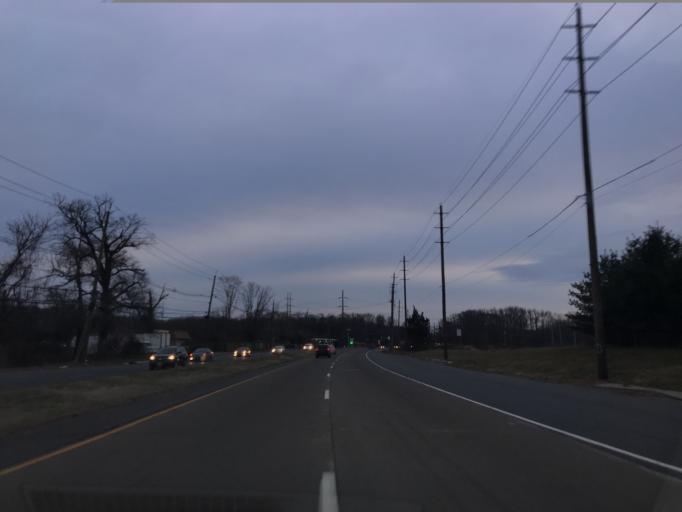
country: US
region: New Jersey
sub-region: Middlesex County
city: Dayton
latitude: 40.4229
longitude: -74.4970
